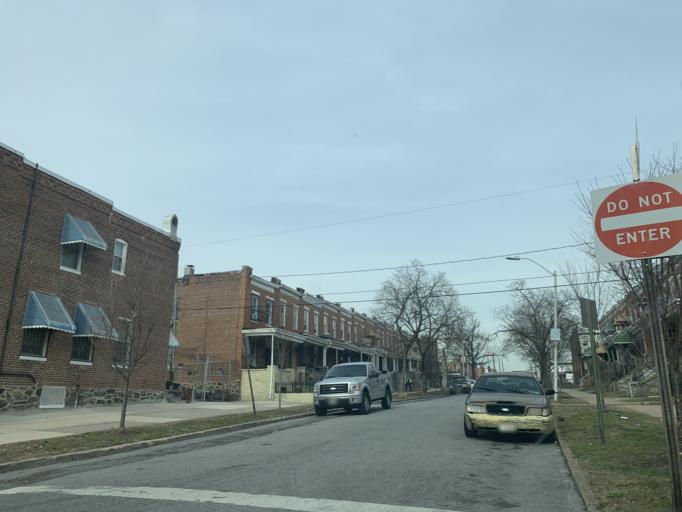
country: US
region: Maryland
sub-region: City of Baltimore
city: Baltimore
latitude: 39.3039
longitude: -76.5783
